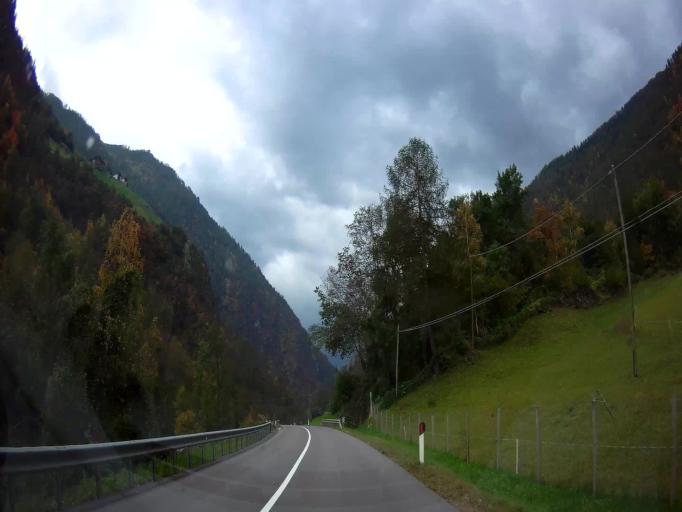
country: IT
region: Trentino-Alto Adige
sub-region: Bolzano
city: Certosa
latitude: 46.6733
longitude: 10.9414
